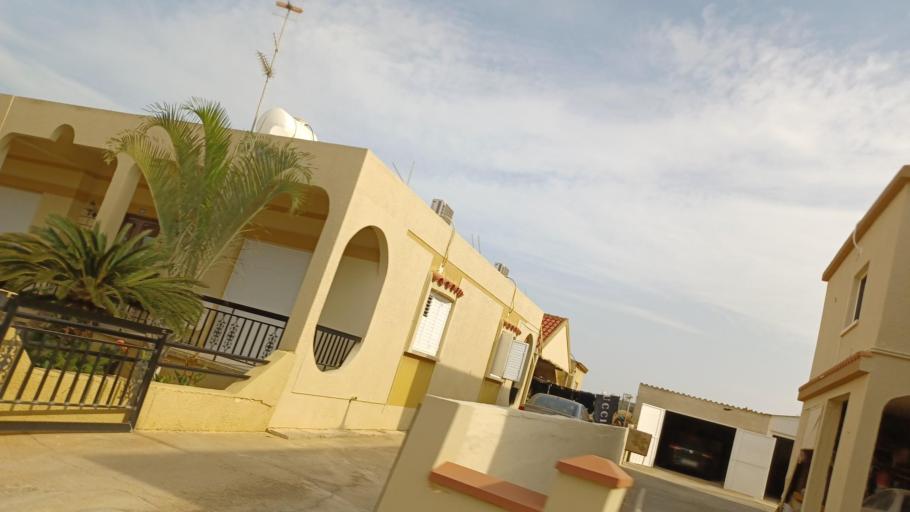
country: CY
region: Ammochostos
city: Frenaros
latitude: 35.0453
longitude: 33.9251
